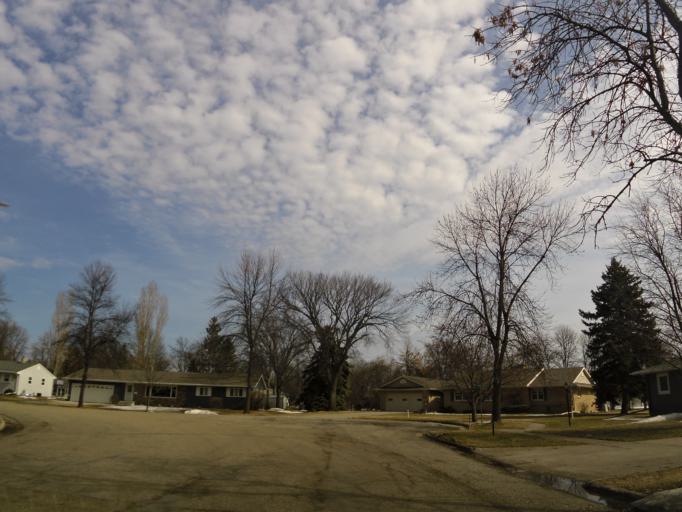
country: US
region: North Dakota
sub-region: Walsh County
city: Grafton
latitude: 48.4090
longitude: -97.4179
